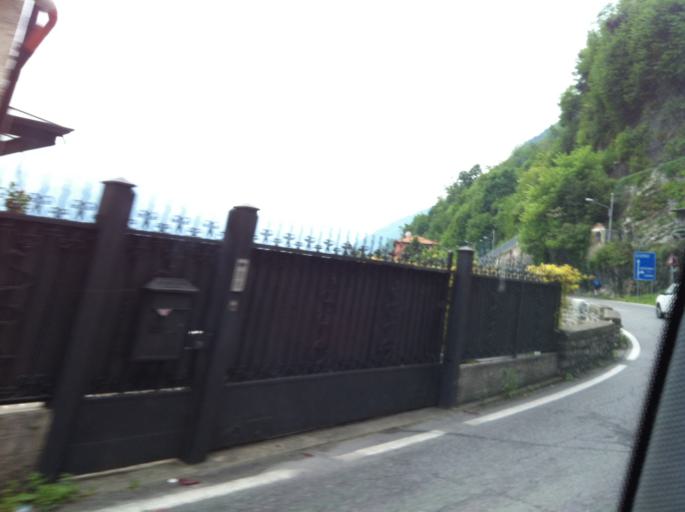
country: IT
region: Lombardy
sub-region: Provincia di Como
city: Argegno
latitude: 45.9399
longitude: 9.1281
